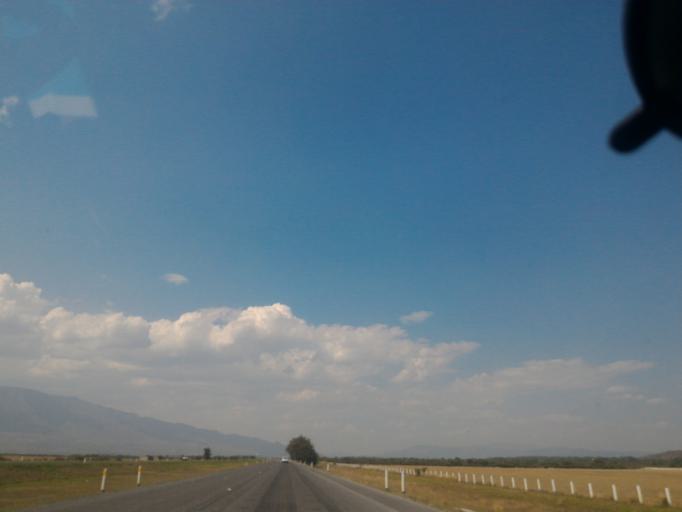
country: MX
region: Jalisco
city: Atoyac
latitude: 19.9472
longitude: -103.5315
